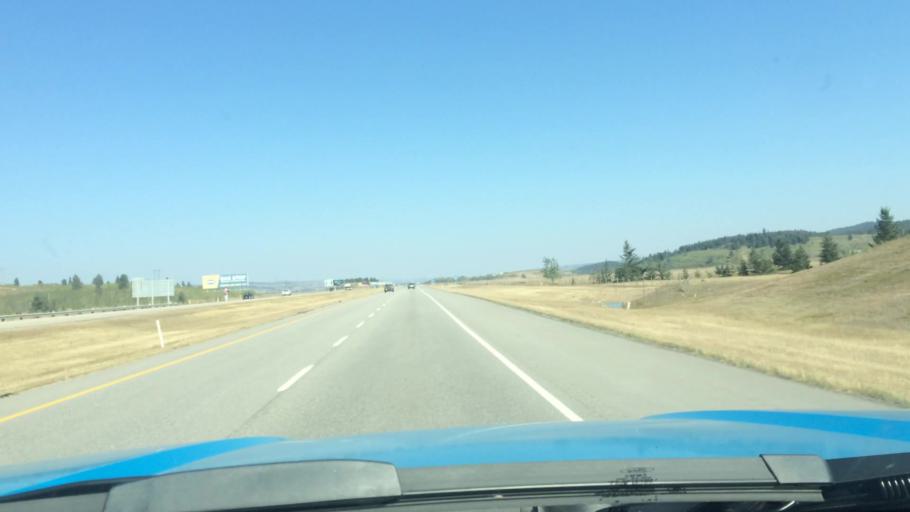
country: CA
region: Alberta
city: Canmore
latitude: 51.1145
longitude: -114.9933
